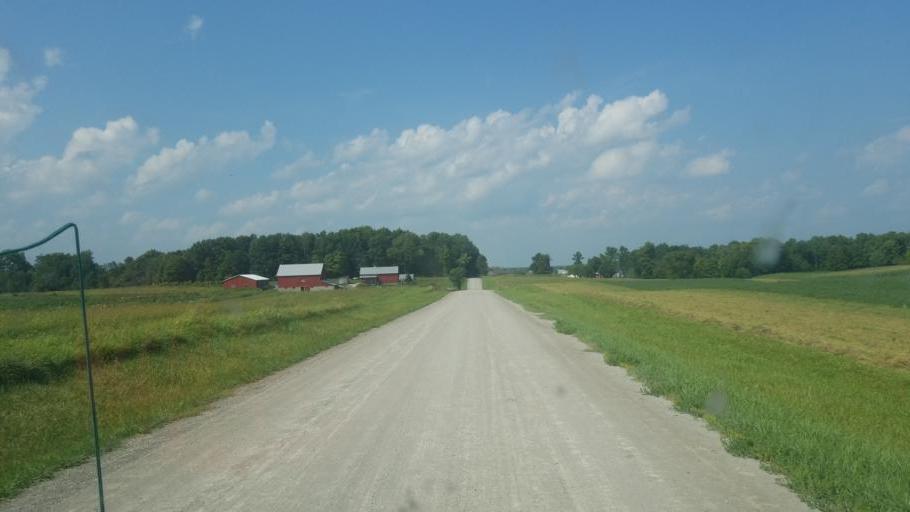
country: US
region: Ohio
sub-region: Wayne County
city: West Salem
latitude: 41.0587
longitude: -82.1446
